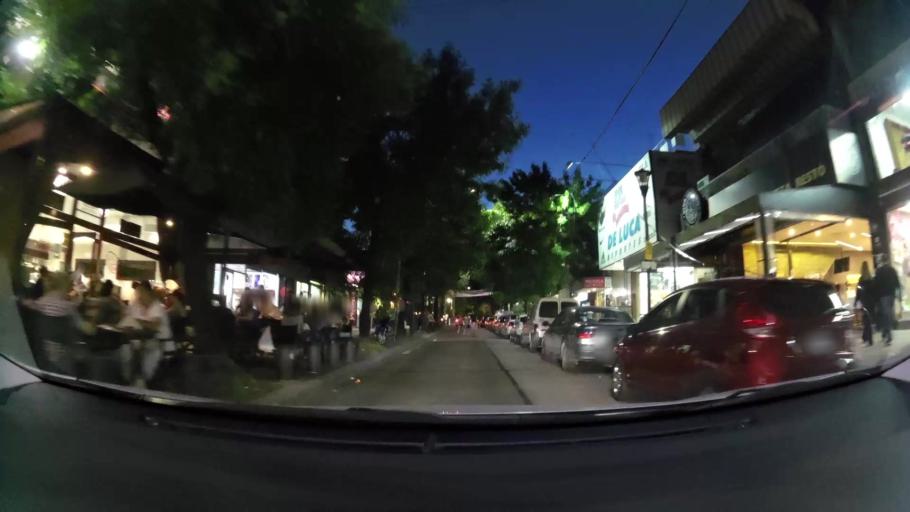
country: AR
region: Buenos Aires F.D.
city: Villa Lugano
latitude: -34.6876
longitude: -58.4775
